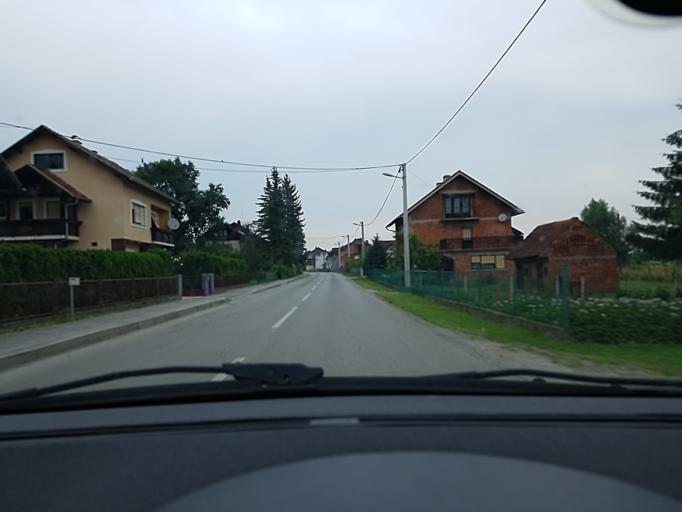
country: HR
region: Zagrebacka
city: Jakovlje
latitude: 45.9927
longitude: 15.8446
